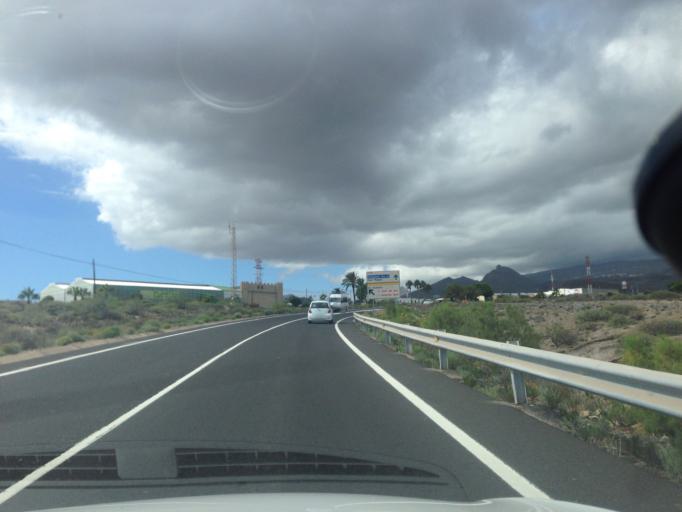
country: ES
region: Canary Islands
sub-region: Provincia de Santa Cruz de Tenerife
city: San Miguel
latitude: 28.0457
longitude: -16.6092
